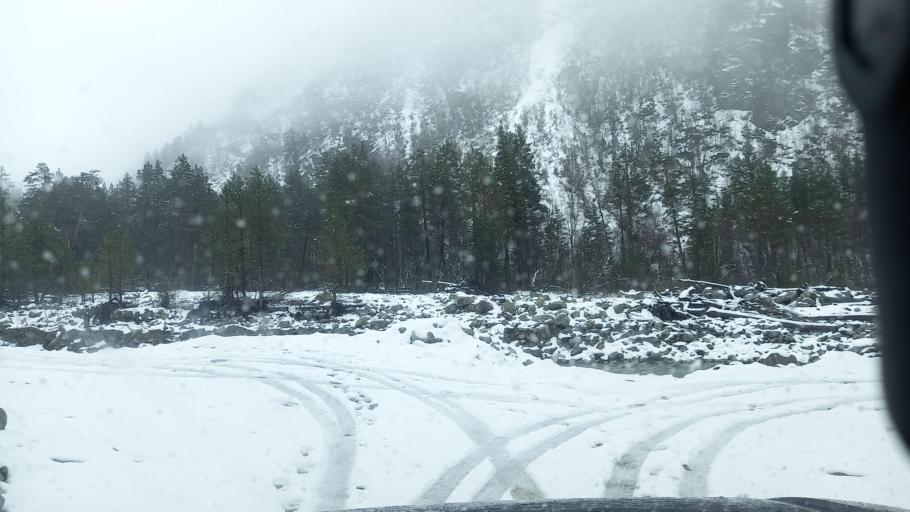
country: RU
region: Kabardino-Balkariya
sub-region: El'brusskiy Rayon
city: El'brus
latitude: 43.2178
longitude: 42.6938
